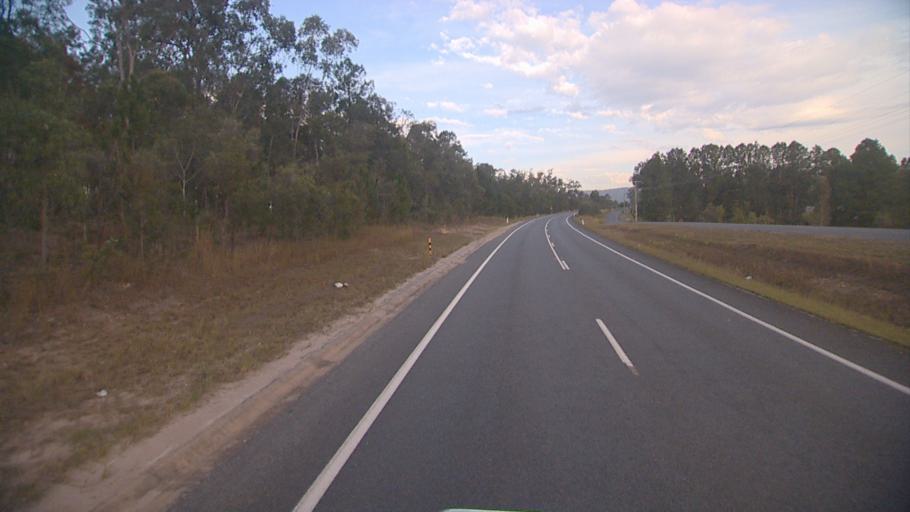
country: AU
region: Queensland
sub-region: Logan
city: Cedar Vale
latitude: -27.8419
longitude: 153.1171
